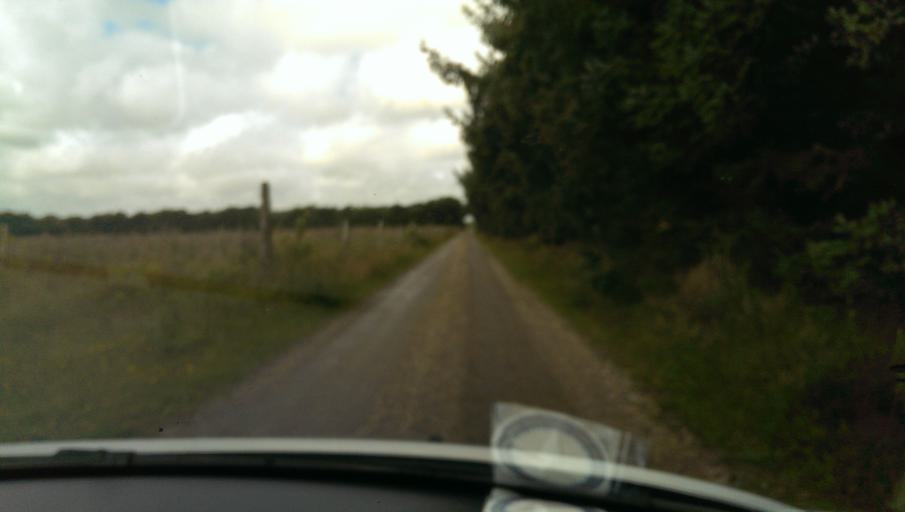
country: DK
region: South Denmark
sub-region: Varde Kommune
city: Varde
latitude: 55.6066
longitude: 8.4500
